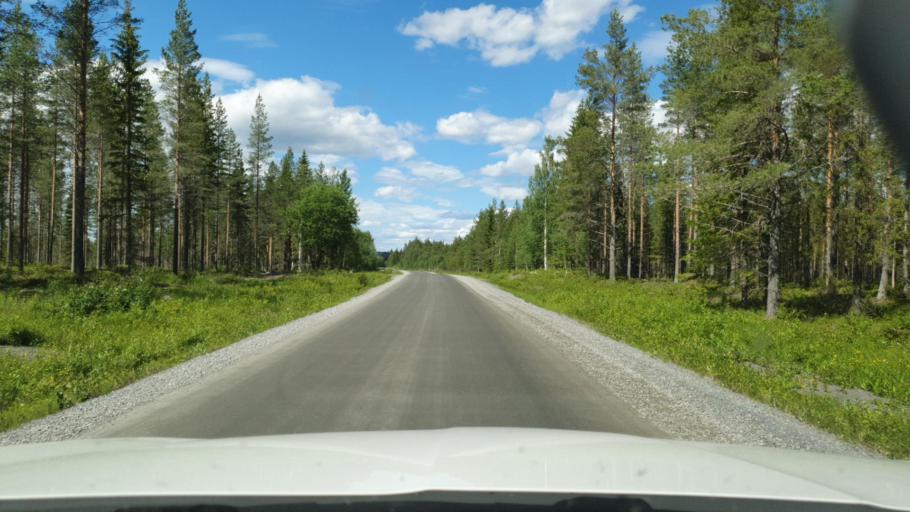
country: SE
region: Vaesterbotten
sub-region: Skelleftea Kommun
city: Forsbacka
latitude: 64.8036
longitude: 20.5022
